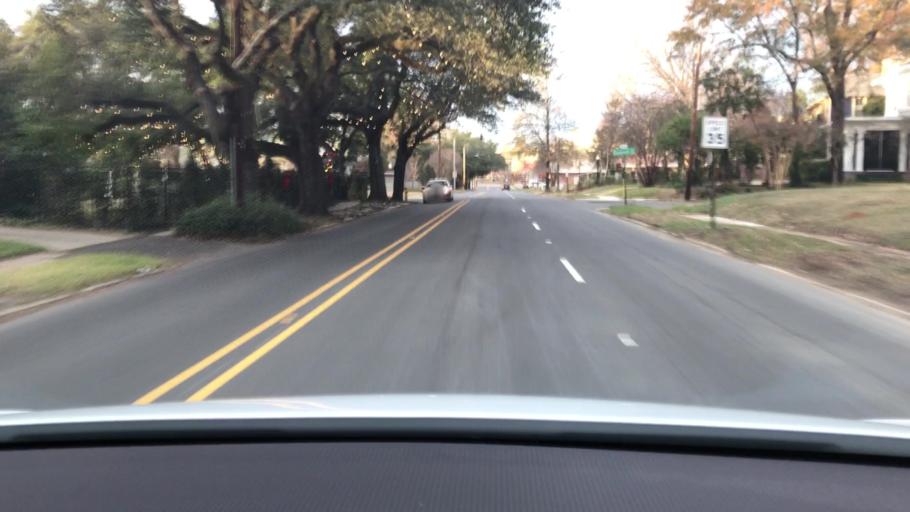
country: US
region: Louisiana
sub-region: Bossier Parish
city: Bossier City
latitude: 32.4895
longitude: -93.7504
